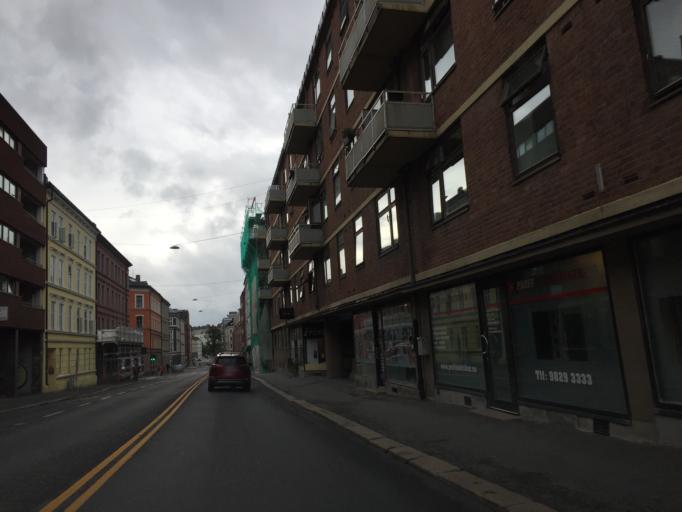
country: NO
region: Oslo
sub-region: Oslo
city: Oslo
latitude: 59.9289
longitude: 10.7666
